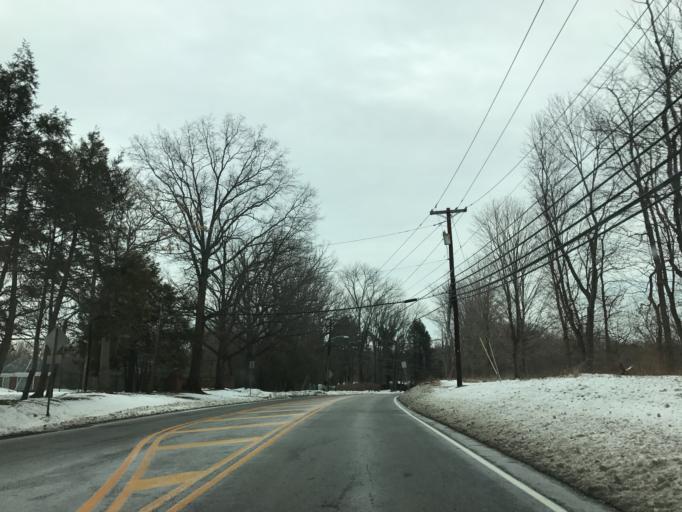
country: US
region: New Jersey
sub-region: Mercer County
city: Princeton
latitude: 40.3307
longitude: -74.6884
